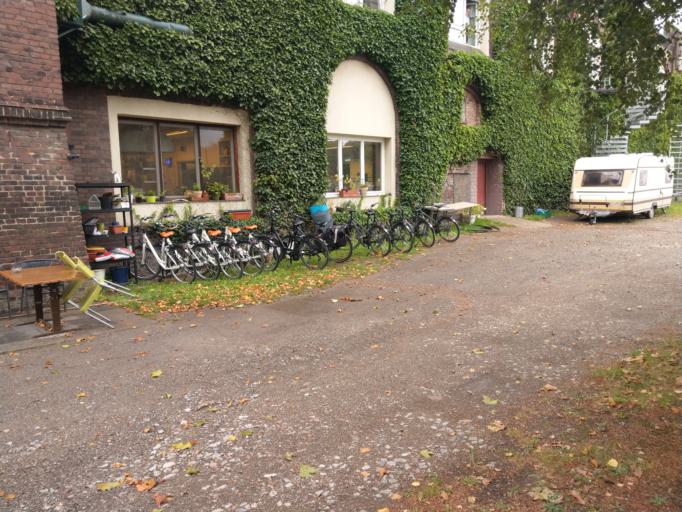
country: DE
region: North Rhine-Westphalia
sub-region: Regierungsbezirk Munster
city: Gelsenkirchen
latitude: 51.4738
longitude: 7.0841
